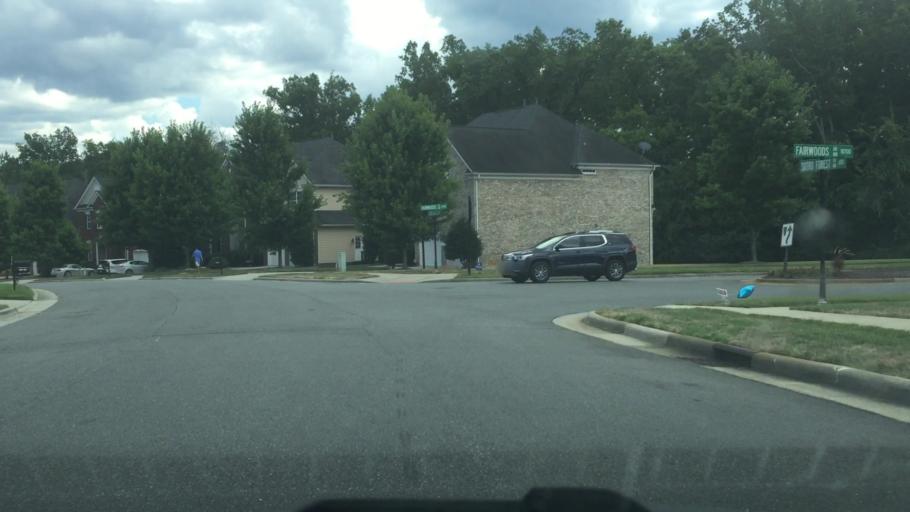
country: US
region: North Carolina
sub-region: Mecklenburg County
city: Huntersville
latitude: 35.4052
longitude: -80.7541
